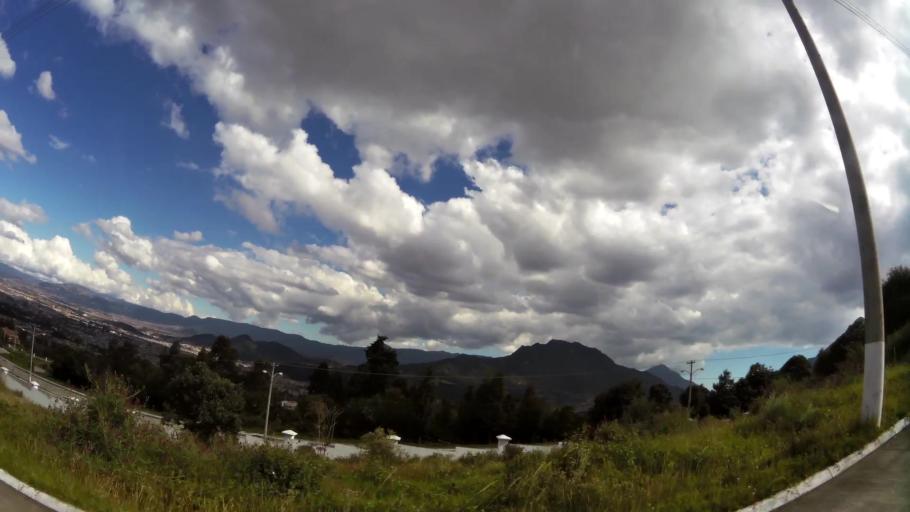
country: GT
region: Quetzaltenango
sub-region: Municipio de La Esperanza
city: La Esperanza
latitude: 14.8346
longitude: -91.5584
